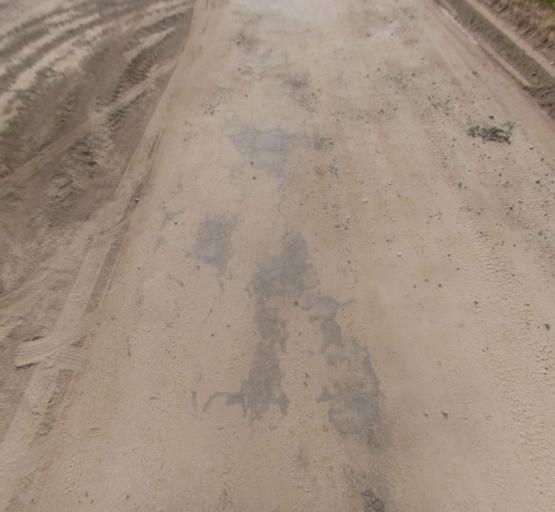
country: US
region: California
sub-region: Madera County
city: Chowchilla
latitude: 37.1417
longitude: -120.2939
